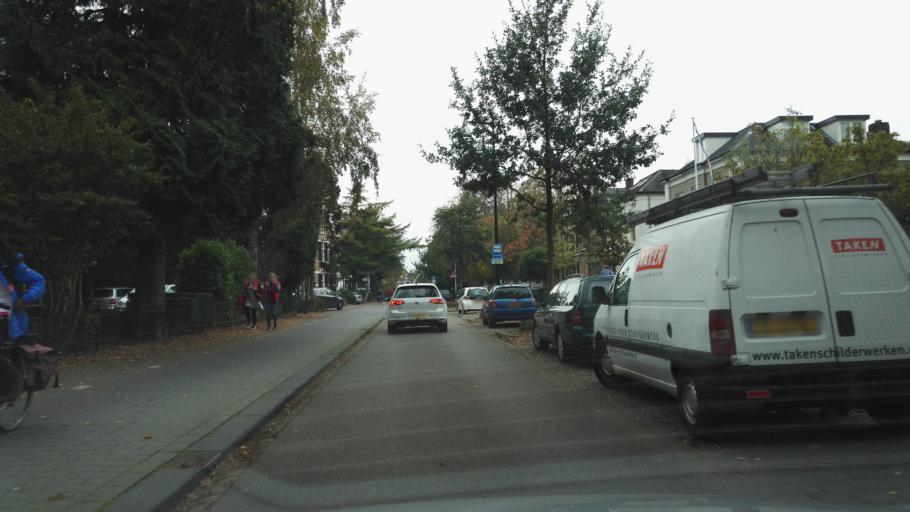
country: NL
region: Gelderland
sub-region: Gemeente Apeldoorn
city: Apeldoorn
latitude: 52.2201
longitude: 5.9600
